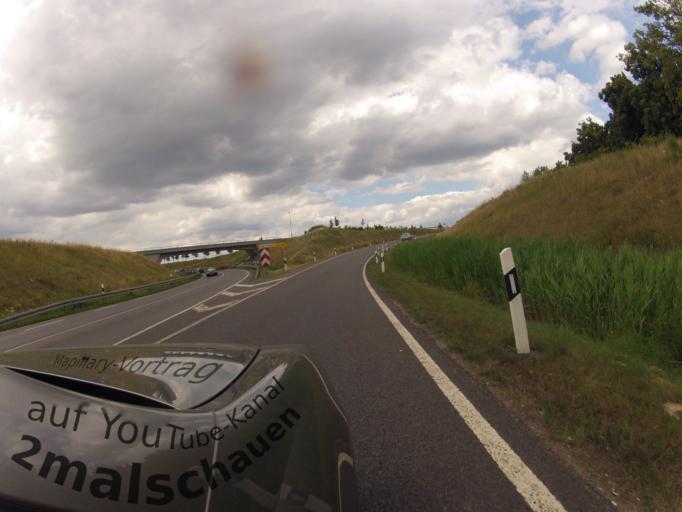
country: DE
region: Mecklenburg-Vorpommern
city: Anklam
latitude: 53.8821
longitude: 13.6929
